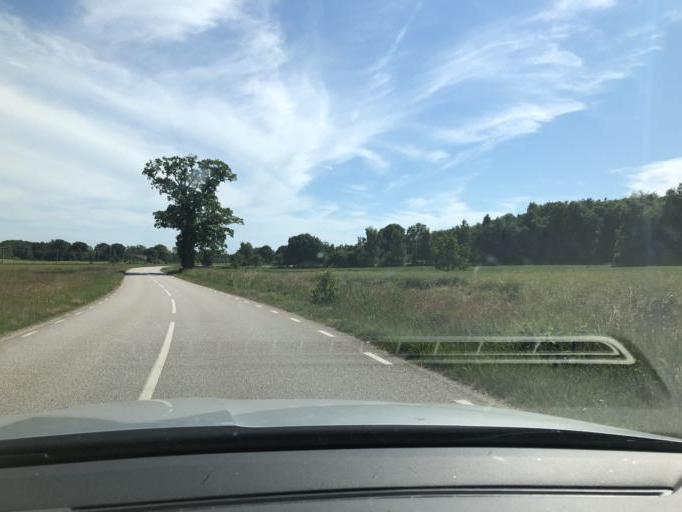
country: SE
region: Blekinge
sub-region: Solvesborgs Kommun
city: Soelvesborg
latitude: 56.0729
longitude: 14.6101
